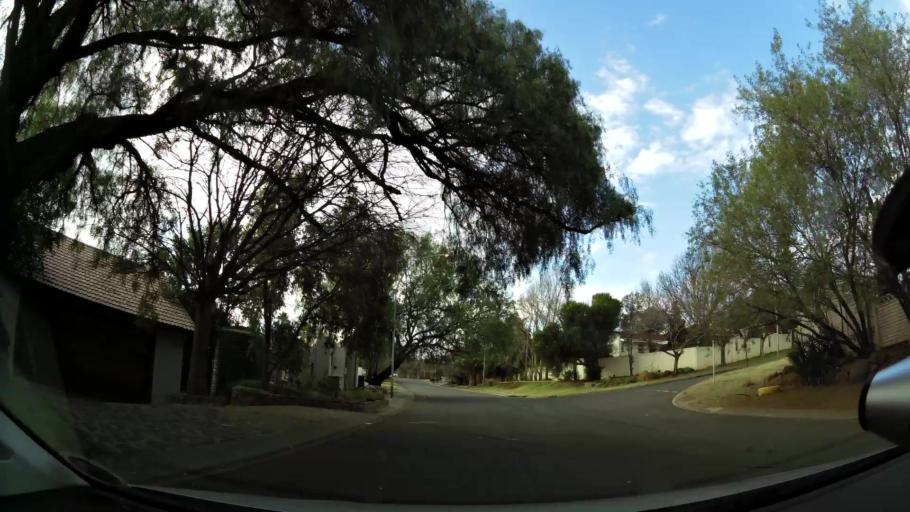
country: ZA
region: Orange Free State
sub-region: Mangaung Metropolitan Municipality
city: Bloemfontein
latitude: -29.0869
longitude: 26.1984
